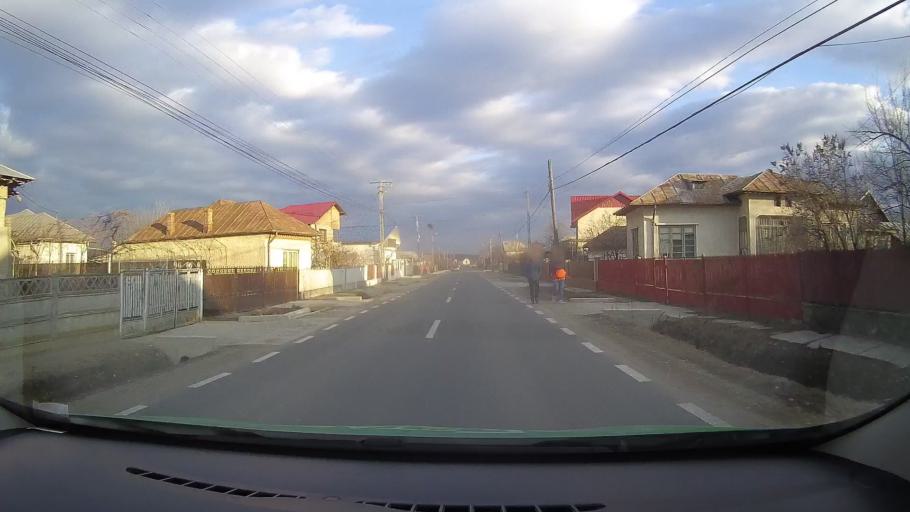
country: RO
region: Dambovita
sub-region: Comuna I. L. Caragiale
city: Ghirdoveni
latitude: 44.9422
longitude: 25.6687
